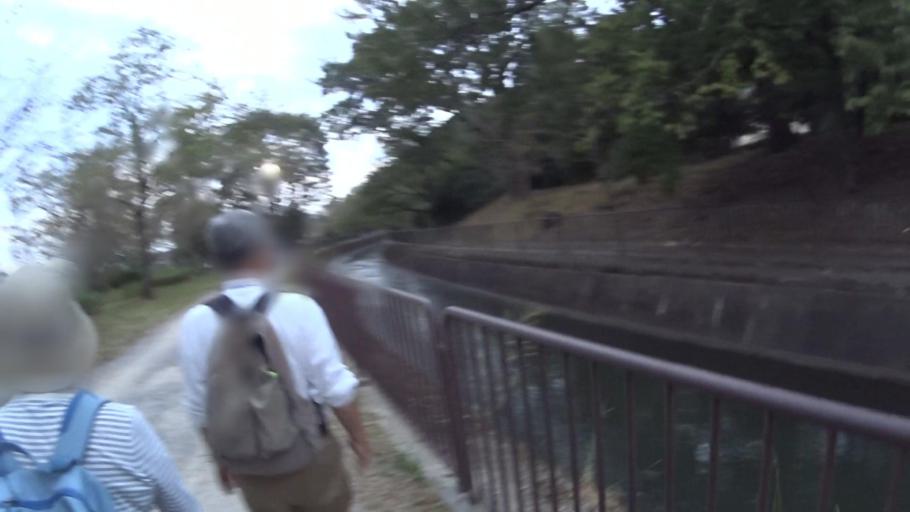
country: JP
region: Osaka
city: Kaizuka
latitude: 34.4451
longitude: 135.2777
